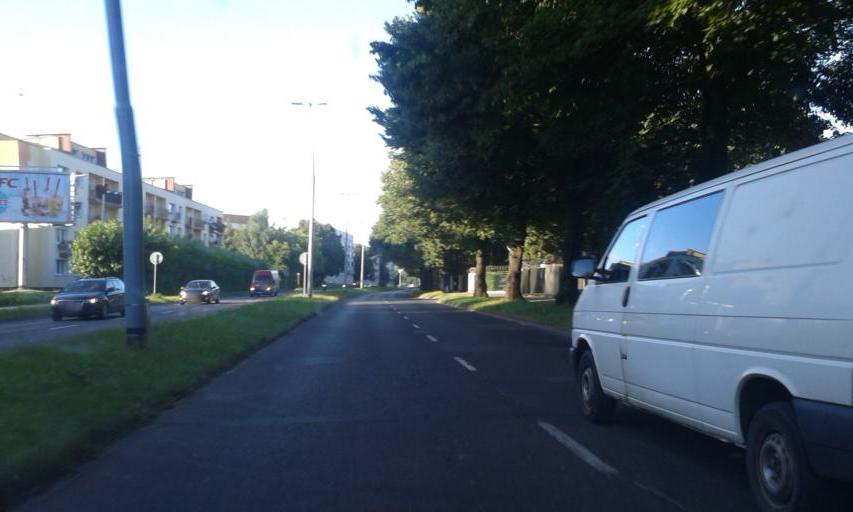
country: PL
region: West Pomeranian Voivodeship
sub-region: Koszalin
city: Koszalin
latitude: 54.1863
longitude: 16.2063
